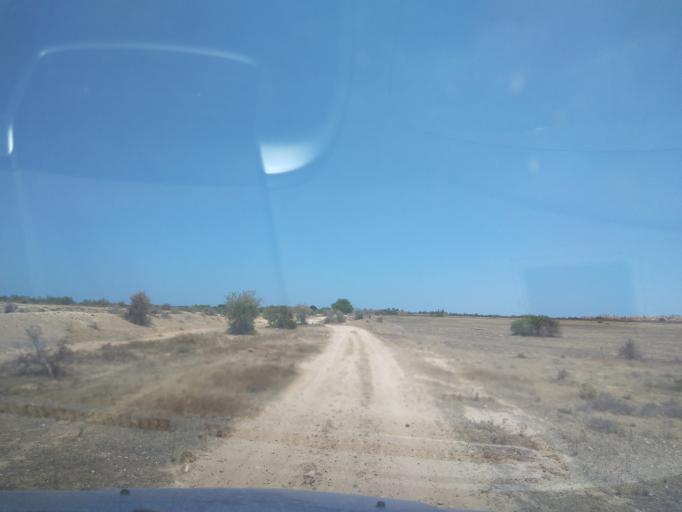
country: TN
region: Susah
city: Harqalah
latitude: 36.1719
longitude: 10.4397
